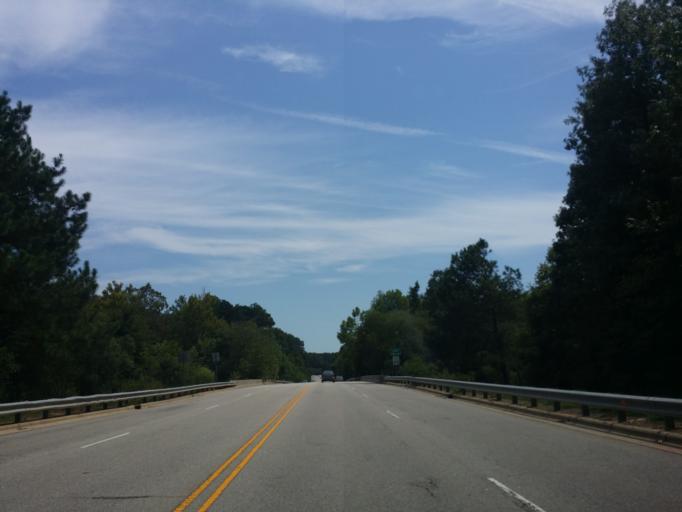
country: US
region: North Carolina
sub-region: Wake County
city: Morrisville
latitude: 35.8313
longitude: -78.8114
